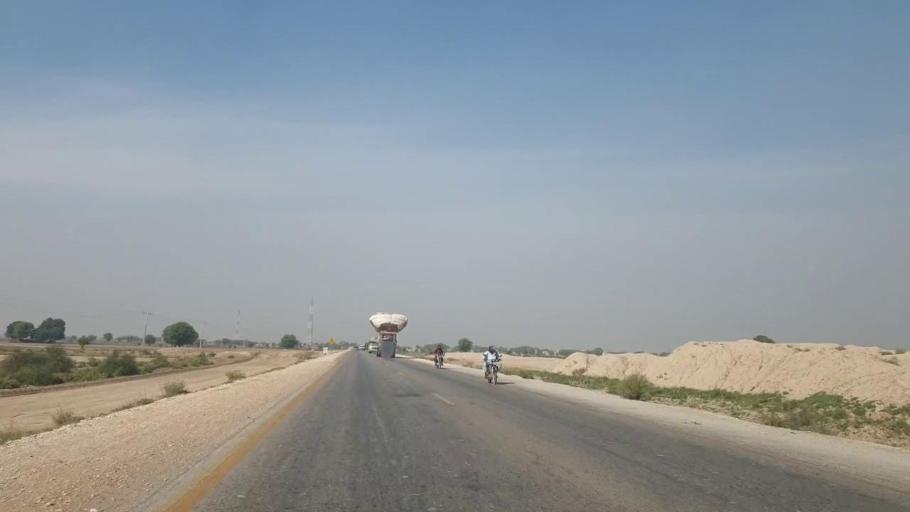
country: PK
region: Sindh
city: Sann
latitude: 25.9758
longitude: 68.1863
